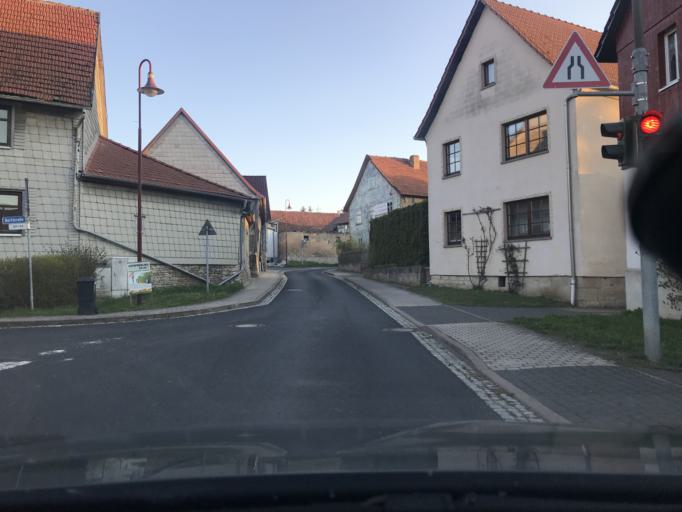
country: DE
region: Thuringia
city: Sollstedt
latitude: 51.2717
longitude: 10.5116
